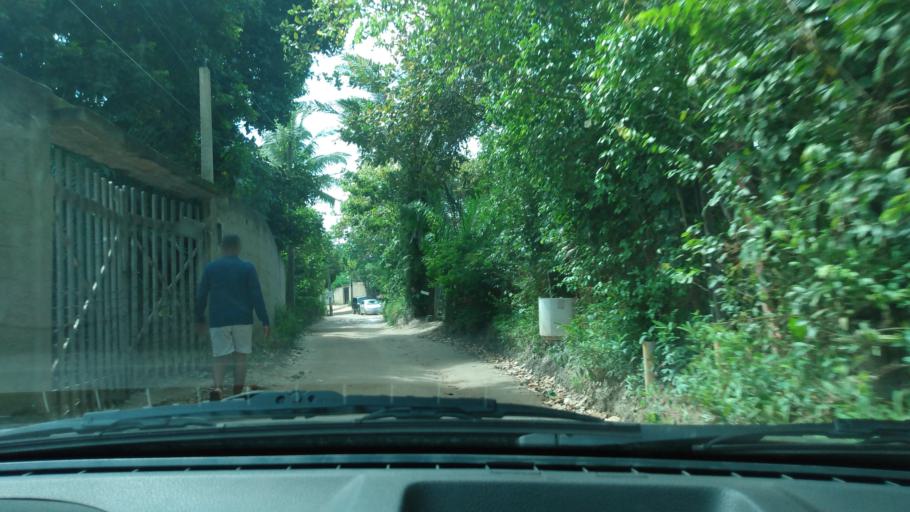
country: BR
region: Pernambuco
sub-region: Cabo De Santo Agostinho
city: Cabo
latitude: -8.3528
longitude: -34.9640
